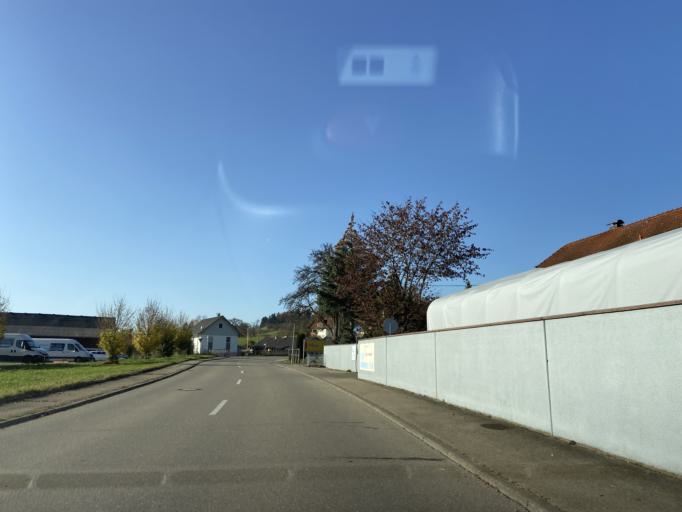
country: DE
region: Baden-Wuerttemberg
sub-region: Tuebingen Region
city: Krauchenwies
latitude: 48.0392
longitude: 9.2801
